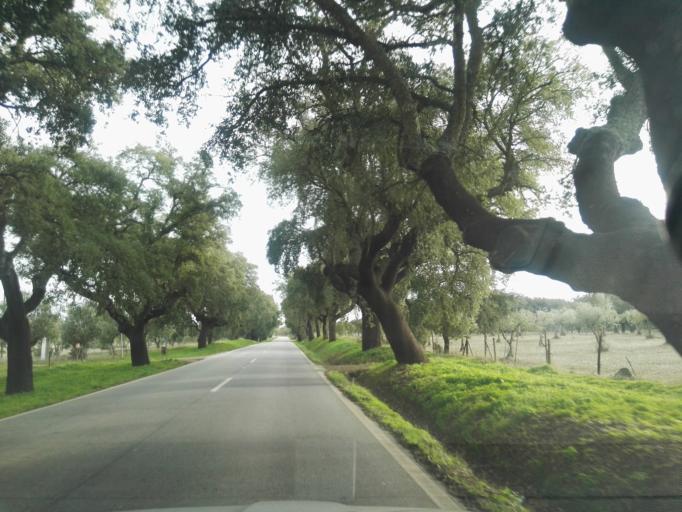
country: PT
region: Portalegre
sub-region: Elvas
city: Elvas
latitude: 38.9395
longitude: -7.1952
